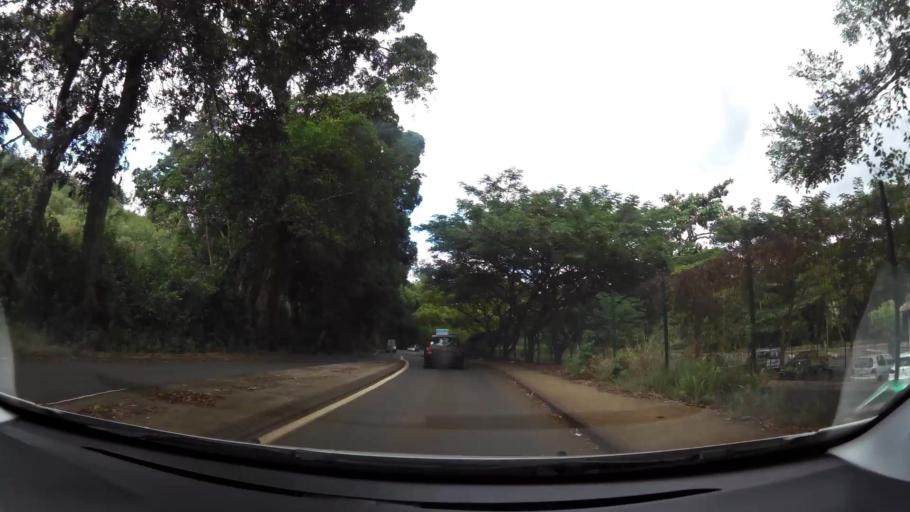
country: YT
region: Dembeni
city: Dembeni
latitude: -12.8389
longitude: 45.1695
